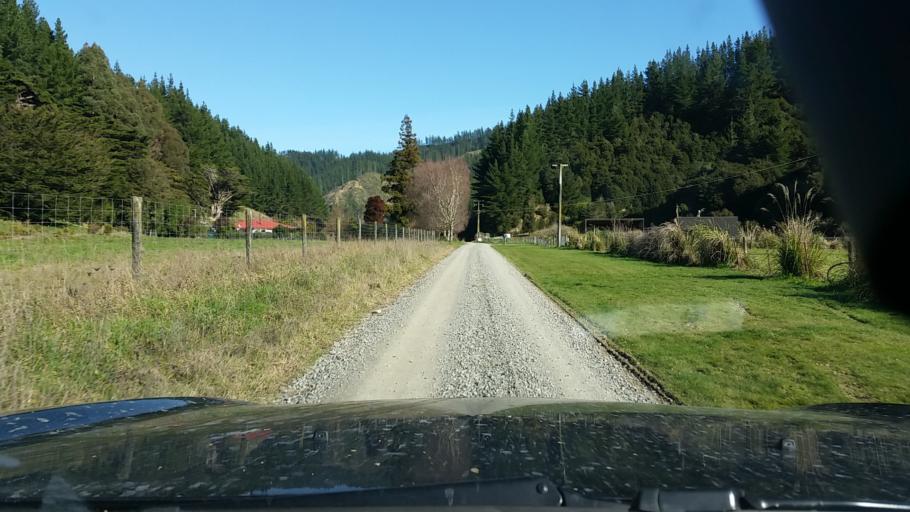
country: NZ
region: Marlborough
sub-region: Marlborough District
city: Blenheim
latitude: -41.4324
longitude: 173.7607
